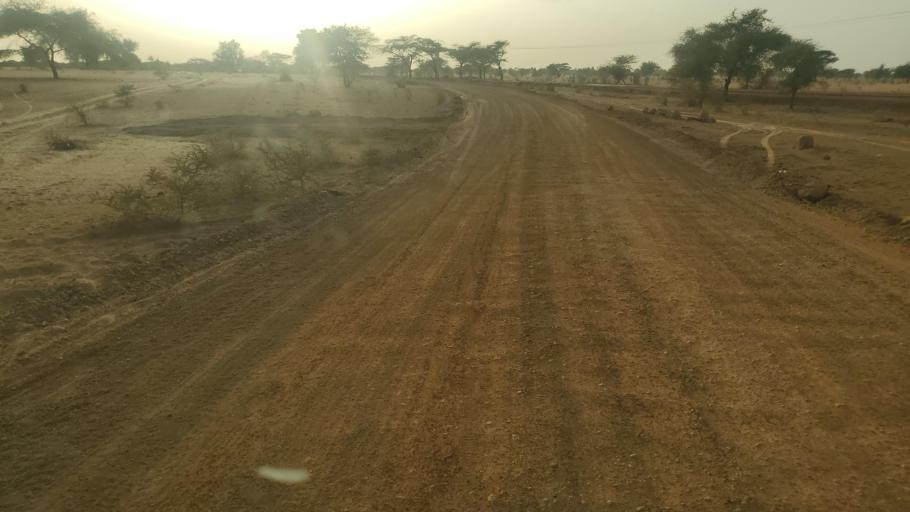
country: SN
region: Louga
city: Dara
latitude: 15.3646
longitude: -15.5571
